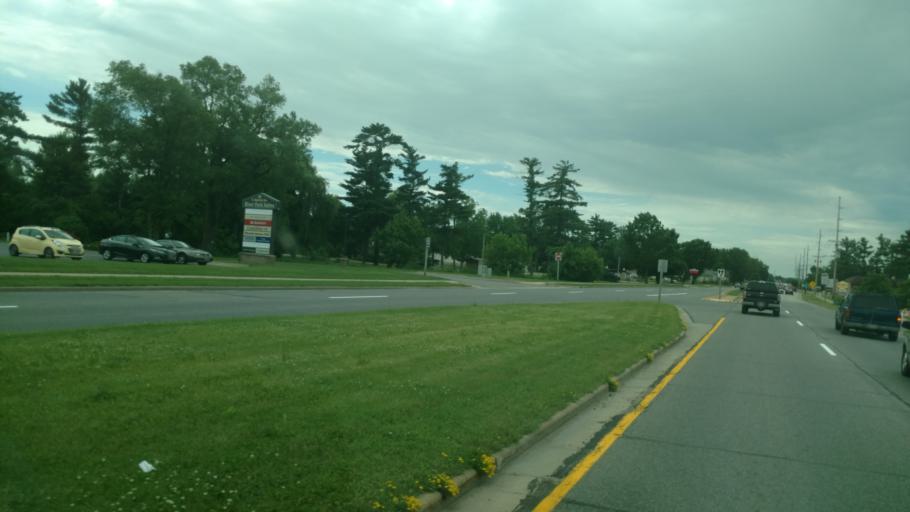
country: US
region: Wisconsin
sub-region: Monroe County
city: Tomah
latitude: 43.9941
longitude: -90.5049
